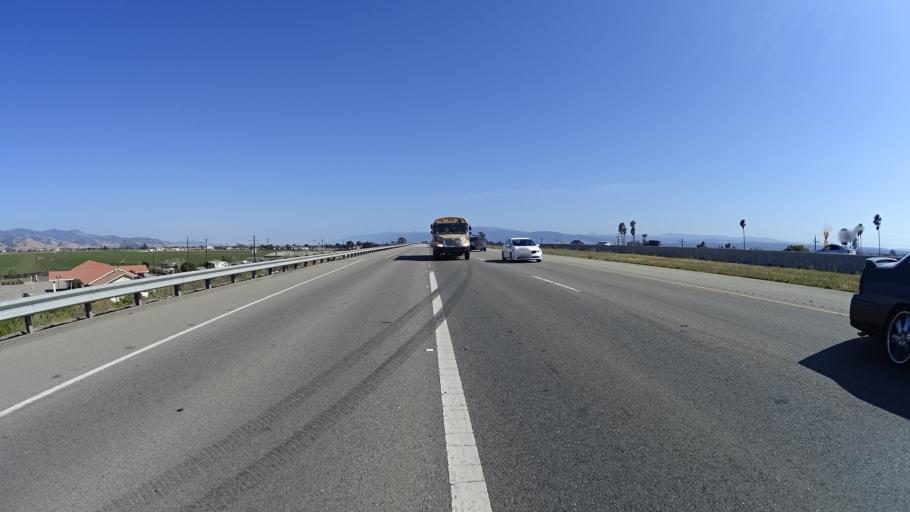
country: US
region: California
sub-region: Monterey County
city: Prunedale
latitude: 36.7398
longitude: -121.6583
